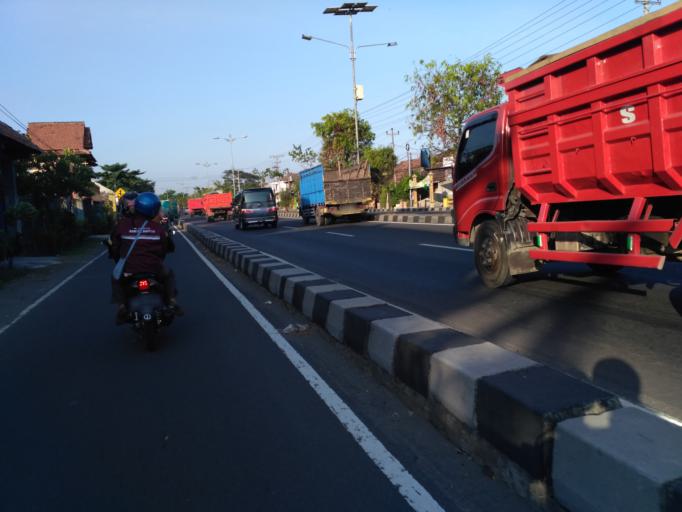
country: ID
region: Daerah Istimewa Yogyakarta
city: Sewon
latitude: -7.8355
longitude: 110.3805
